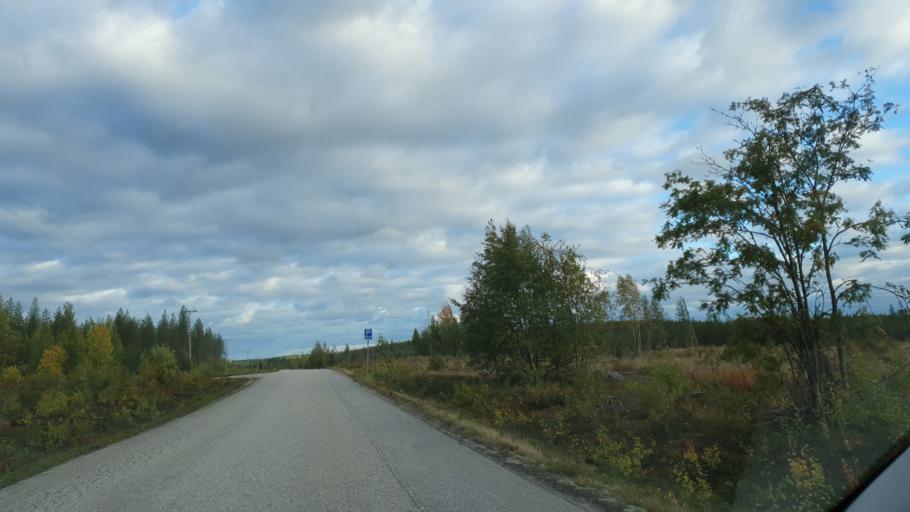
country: FI
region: North Karelia
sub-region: Pielisen Karjala
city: Lieksa
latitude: 63.9200
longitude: 30.1595
